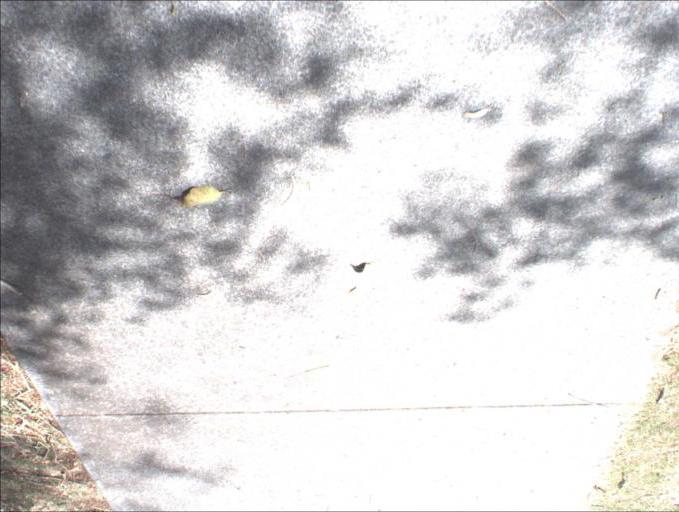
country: AU
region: Queensland
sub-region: Logan
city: Slacks Creek
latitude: -27.6729
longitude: 153.1573
